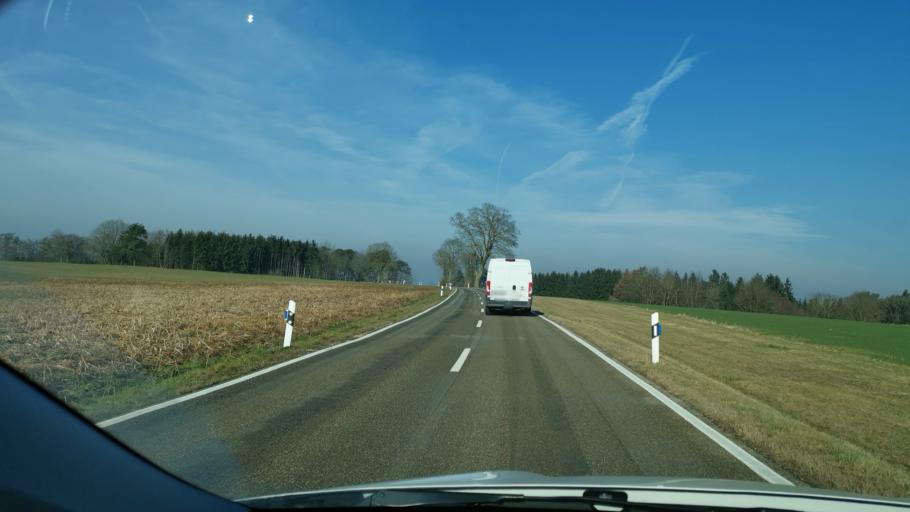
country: DE
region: Bavaria
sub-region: Swabia
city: Holzheim
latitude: 48.6241
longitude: 10.9343
